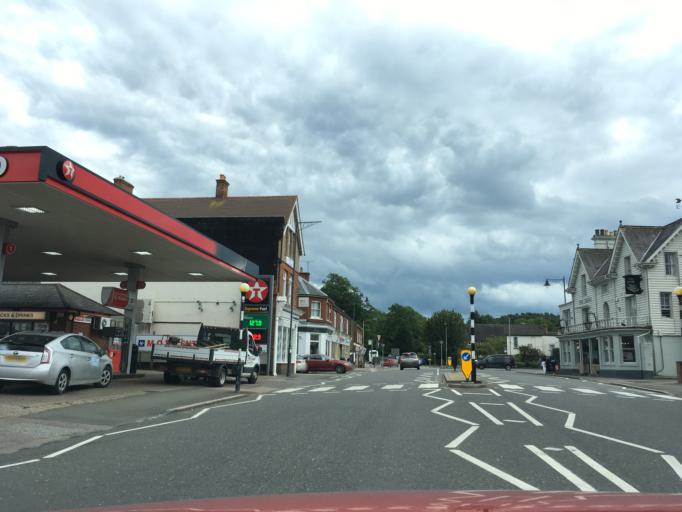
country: GB
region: England
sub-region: Milton Keynes
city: Woburn Sands
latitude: 52.0111
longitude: -0.6468
